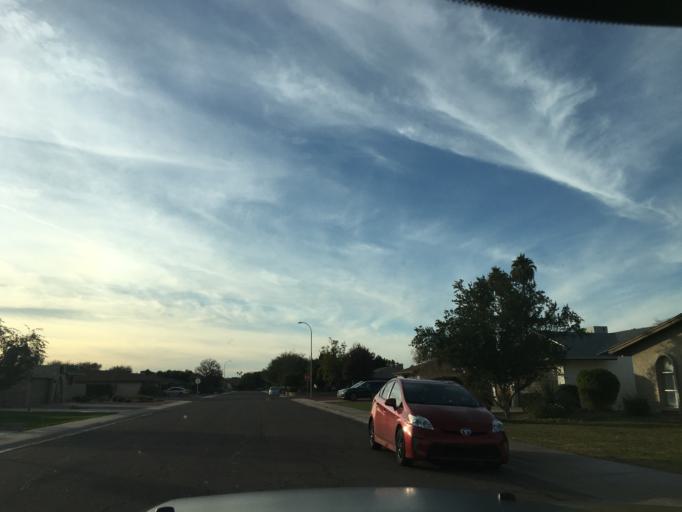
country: US
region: Arizona
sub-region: Maricopa County
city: Tempe
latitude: 33.3718
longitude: -111.9067
